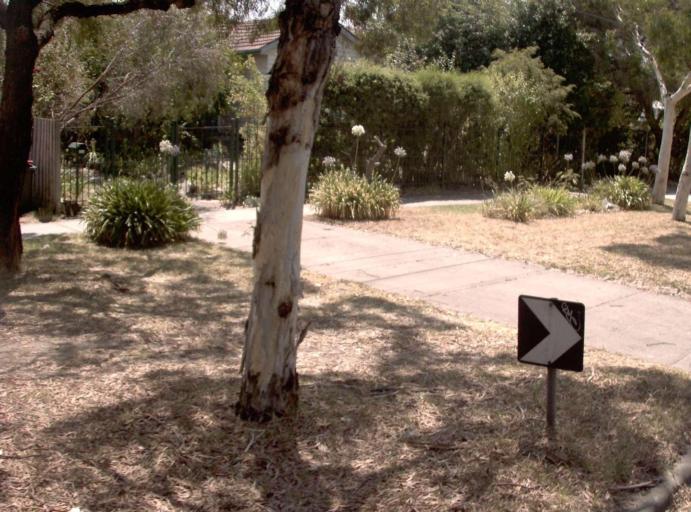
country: AU
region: Victoria
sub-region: Greater Dandenong
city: Springvale
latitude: -37.9282
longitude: 145.1565
